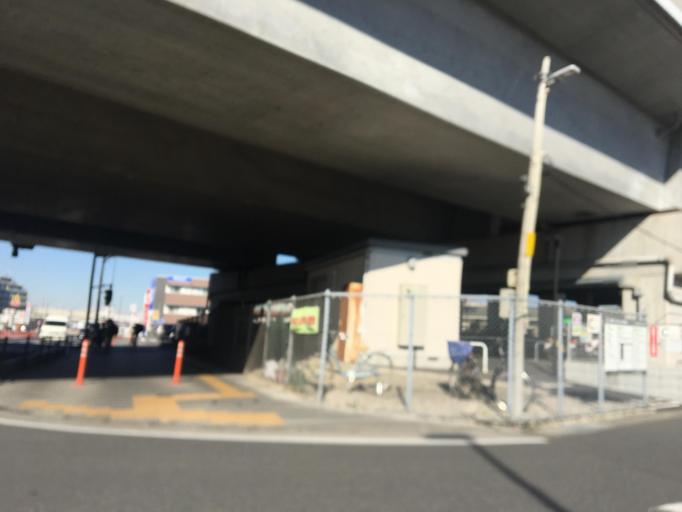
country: JP
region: Saitama
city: Yashio-shi
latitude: 35.8084
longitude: 139.8461
